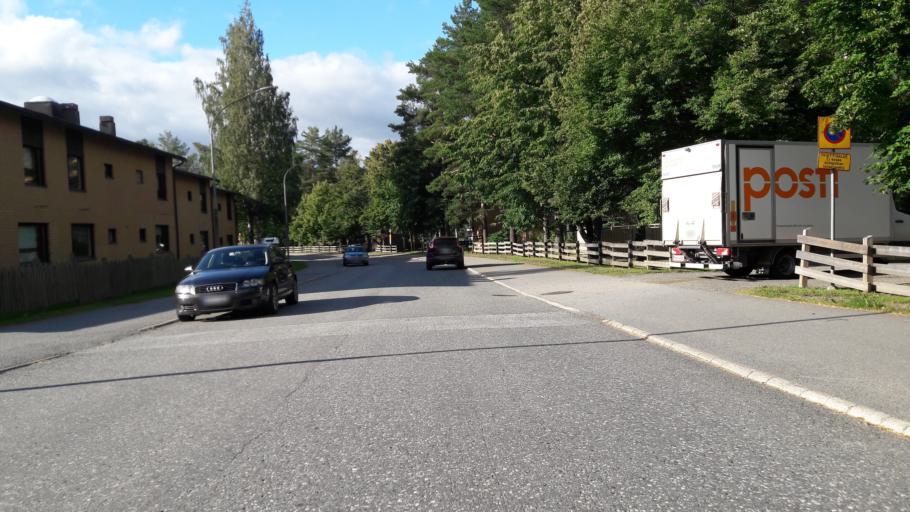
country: FI
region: North Karelia
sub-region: Joensuu
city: Joensuu
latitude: 62.6033
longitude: 29.8000
